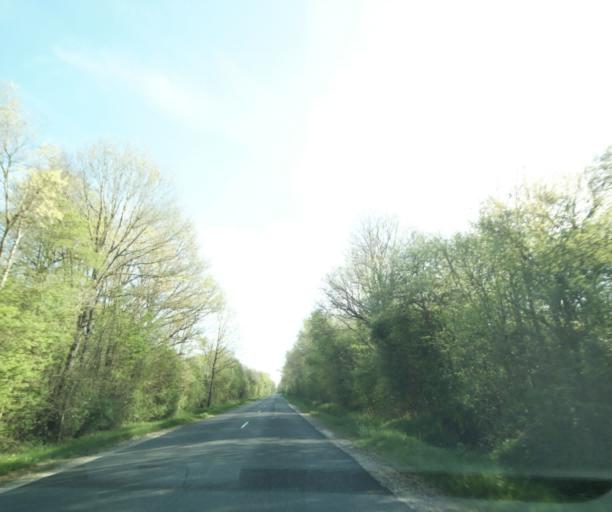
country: FR
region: Ile-de-France
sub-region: Departement de Seine-et-Marne
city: La Chapelle-Gauthier
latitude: 48.4809
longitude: 2.8749
